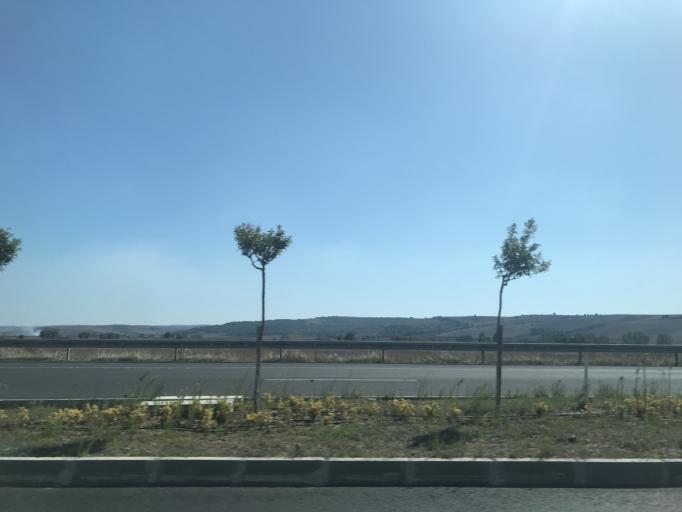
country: TR
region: Tekirdag
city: Muratli
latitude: 41.1633
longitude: 27.5281
